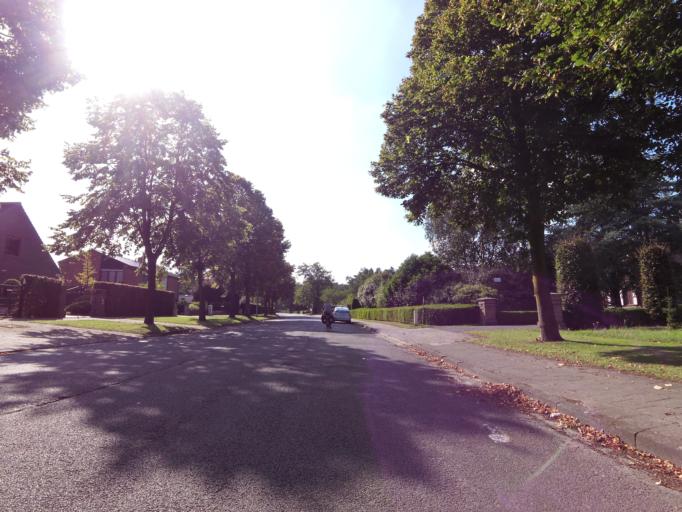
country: BE
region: Flanders
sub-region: Provincie West-Vlaanderen
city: Brugge
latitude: 51.1983
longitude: 3.1690
